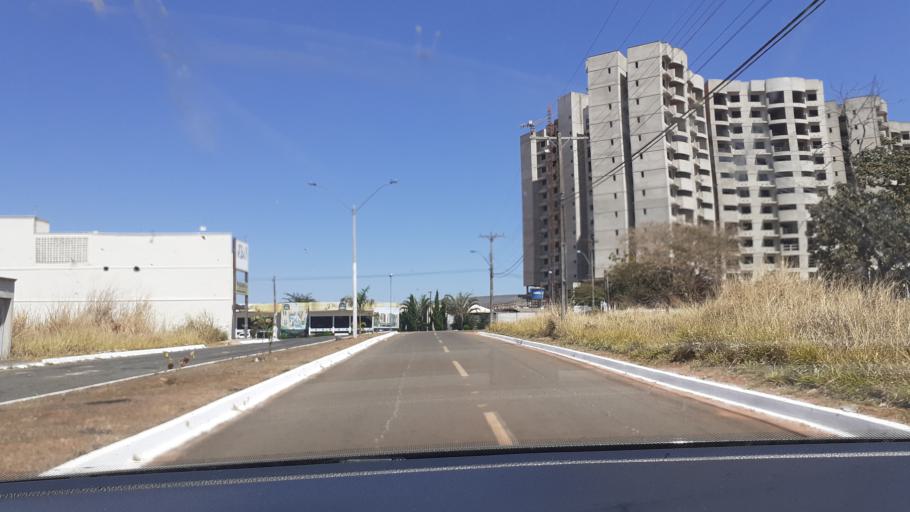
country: BR
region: Goias
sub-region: Caldas Novas
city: Caldas Novas
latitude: -17.7403
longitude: -48.6363
